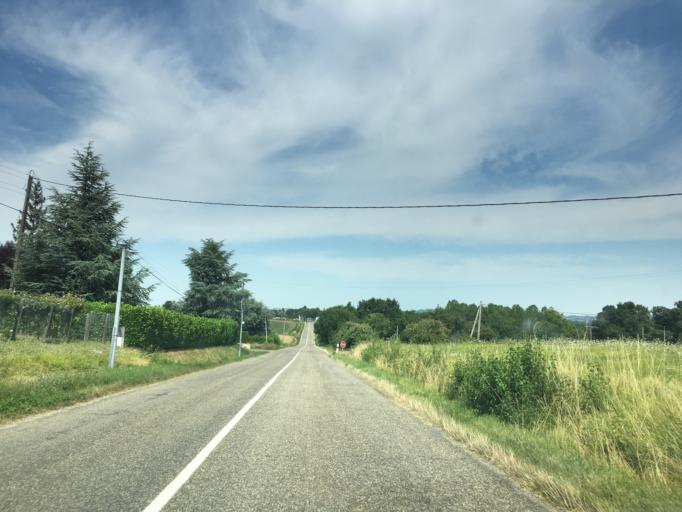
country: FR
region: Midi-Pyrenees
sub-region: Departement du Gers
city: Fleurance
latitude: 43.8809
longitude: 0.7597
